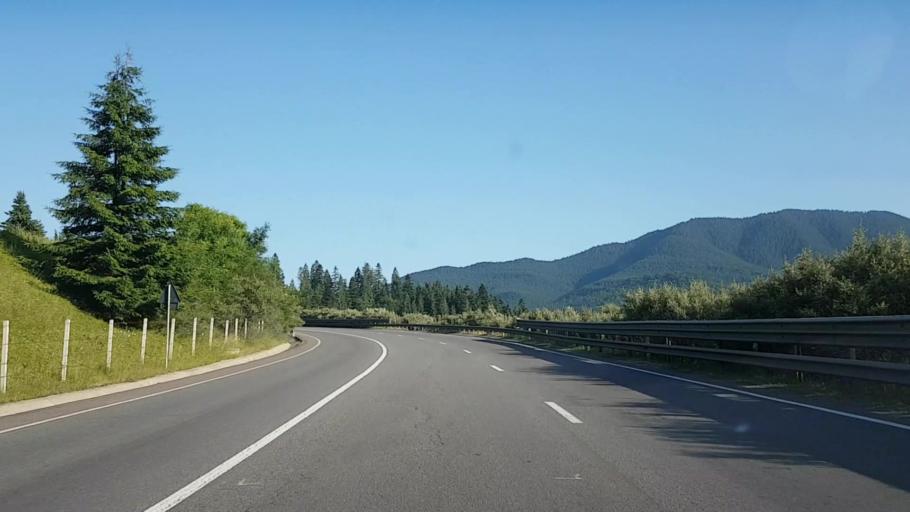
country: RO
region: Bistrita-Nasaud
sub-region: Comuna Lunca Ilvei
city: Lunca Ilvei
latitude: 47.2292
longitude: 24.9670
